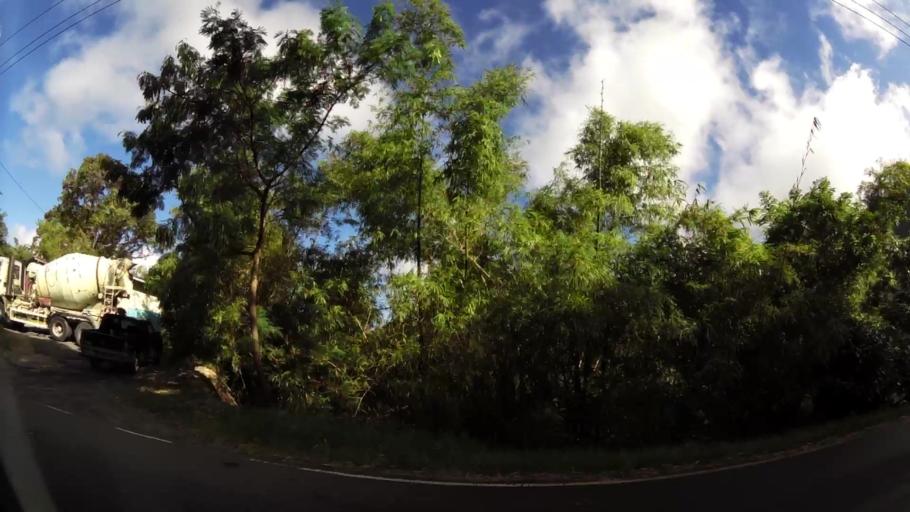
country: LC
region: Soufriere
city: Soufriere
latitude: 13.8687
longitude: -61.0488
